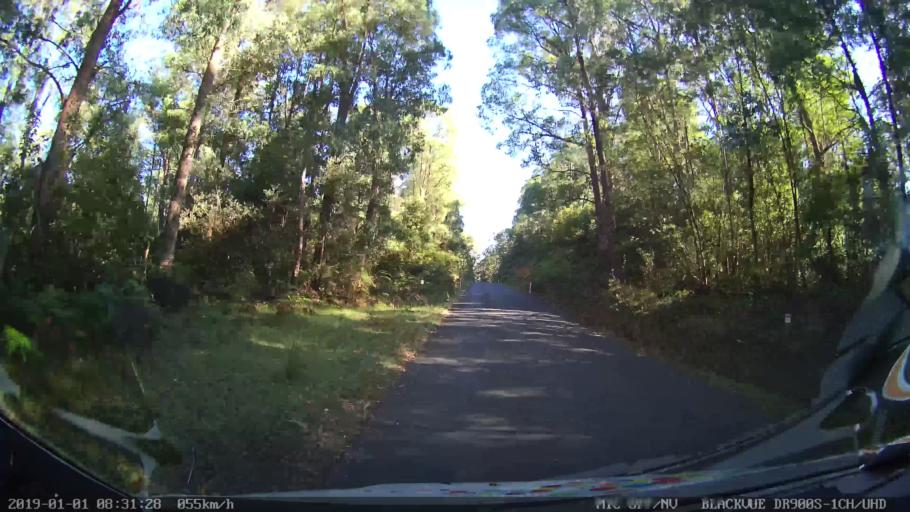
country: AU
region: New South Wales
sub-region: Snowy River
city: Jindabyne
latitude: -36.3701
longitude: 148.2051
